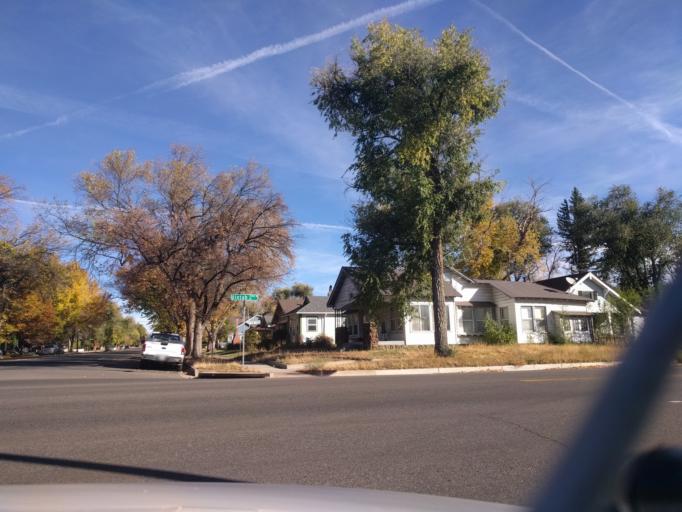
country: US
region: Colorado
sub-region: El Paso County
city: Colorado Springs
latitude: 38.8503
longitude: -104.8154
